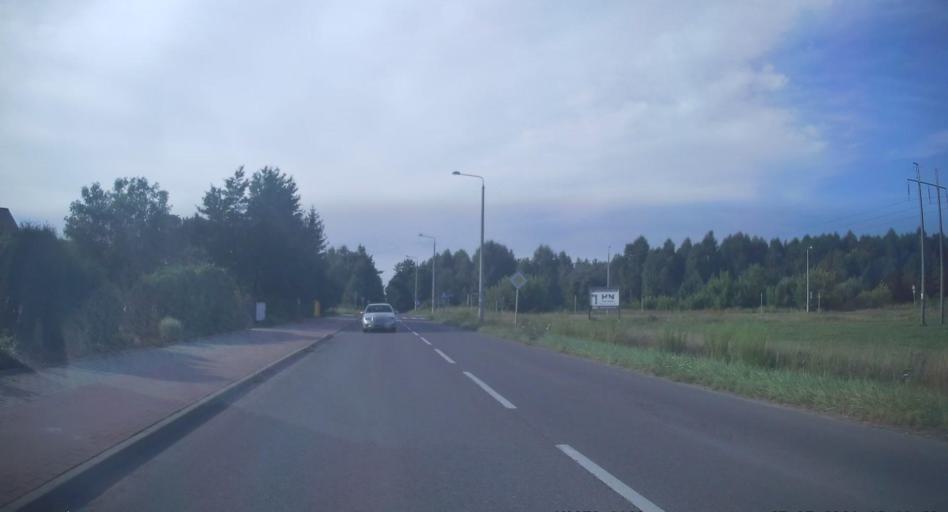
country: PL
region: Swietokrzyskie
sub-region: Powiat konecki
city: Konskie
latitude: 51.2168
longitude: 20.3910
